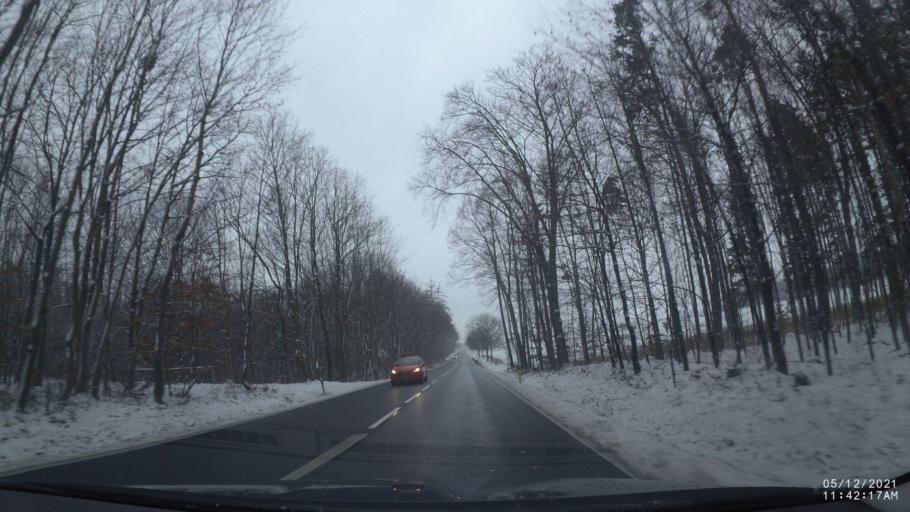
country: CZ
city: Dobruska
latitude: 50.2764
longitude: 16.1899
